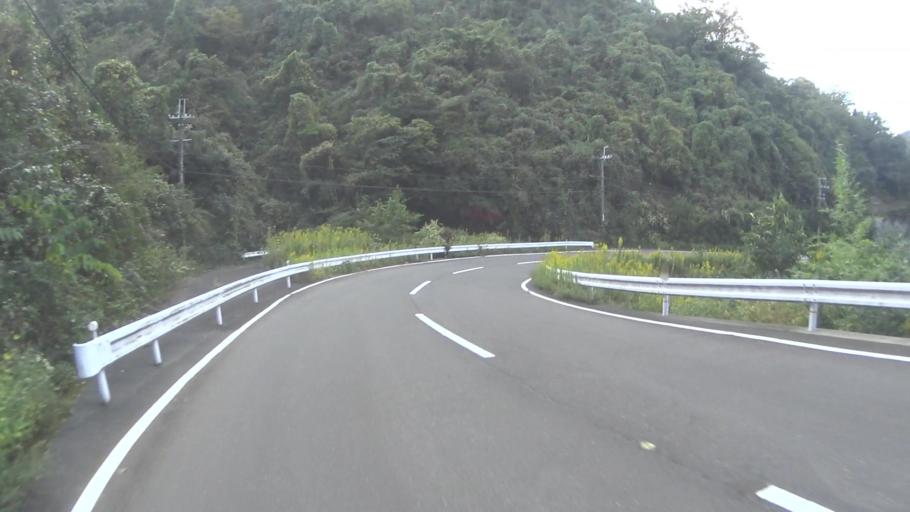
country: JP
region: Kyoto
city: Maizuru
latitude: 35.5555
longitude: 135.4400
